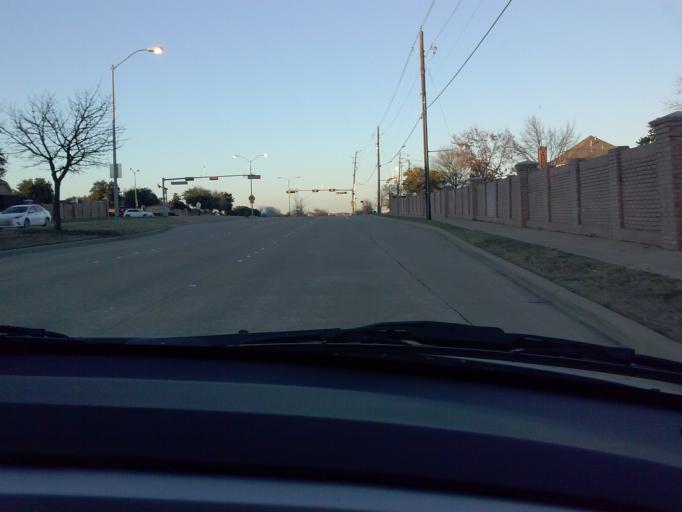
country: US
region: Texas
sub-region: Collin County
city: Allen
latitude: 33.0851
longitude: -96.7498
